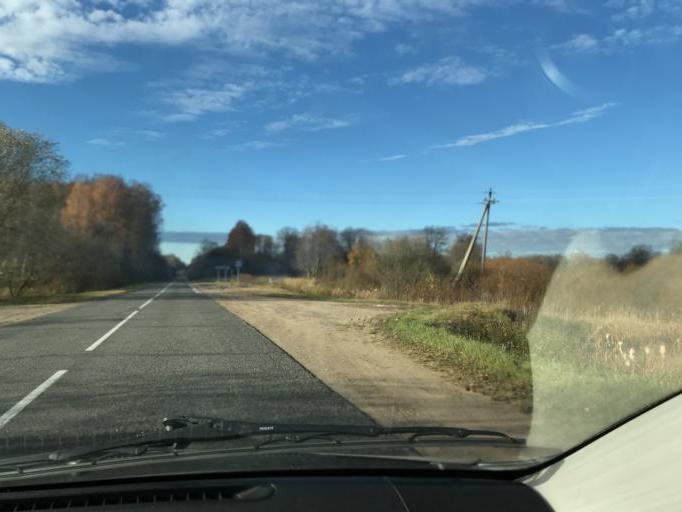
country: BY
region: Vitebsk
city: Haradok
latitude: 55.3999
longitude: 29.7130
